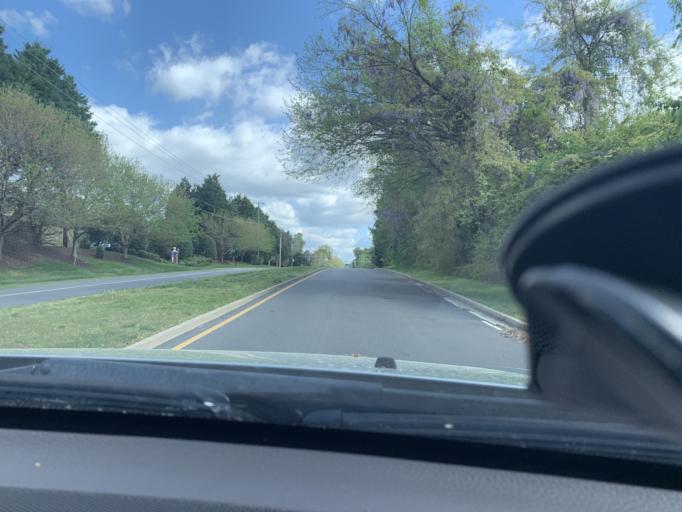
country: US
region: Virginia
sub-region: Henrico County
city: Tuckahoe
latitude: 37.5905
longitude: -77.5993
